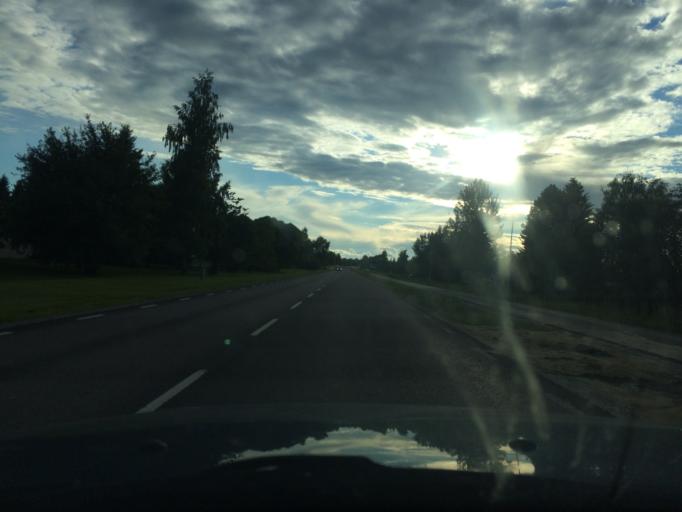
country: SE
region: Norrbotten
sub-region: Pitea Kommun
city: Pitea
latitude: 65.3232
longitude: 21.4595
